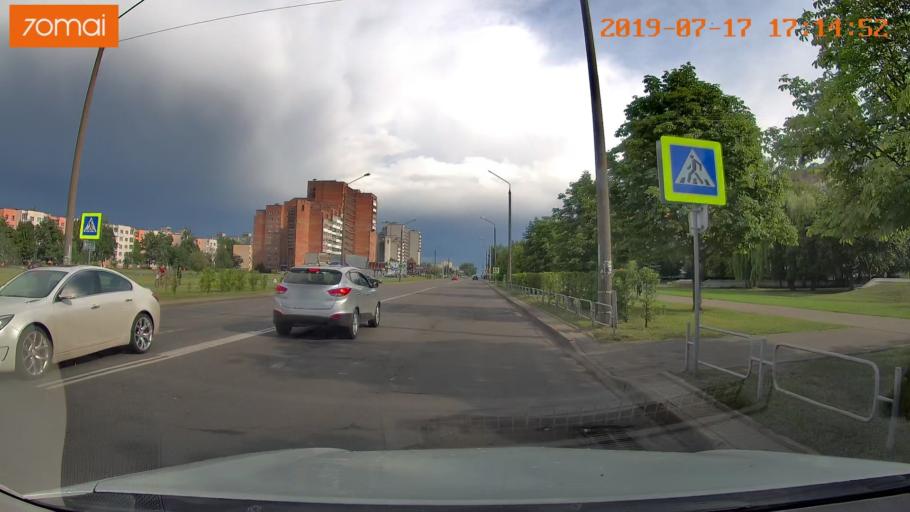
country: BY
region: Mogilev
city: Babruysk
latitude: 53.1732
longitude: 29.1888
